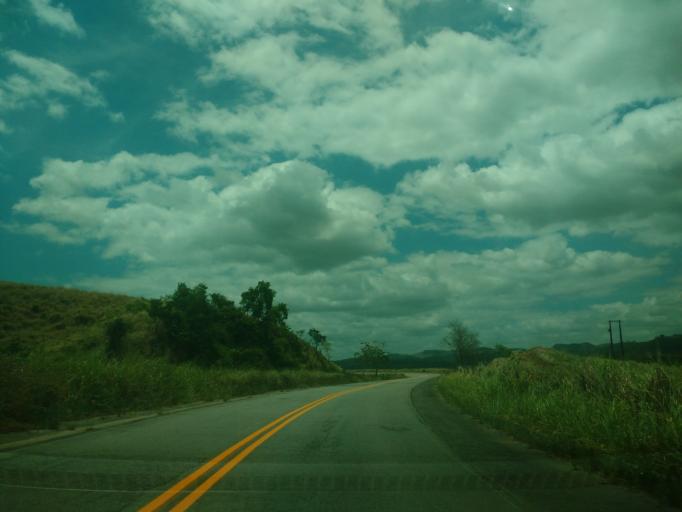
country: BR
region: Alagoas
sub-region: Uniao Dos Palmares
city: Uniao dos Palmares
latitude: -9.1444
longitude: -36.0624
